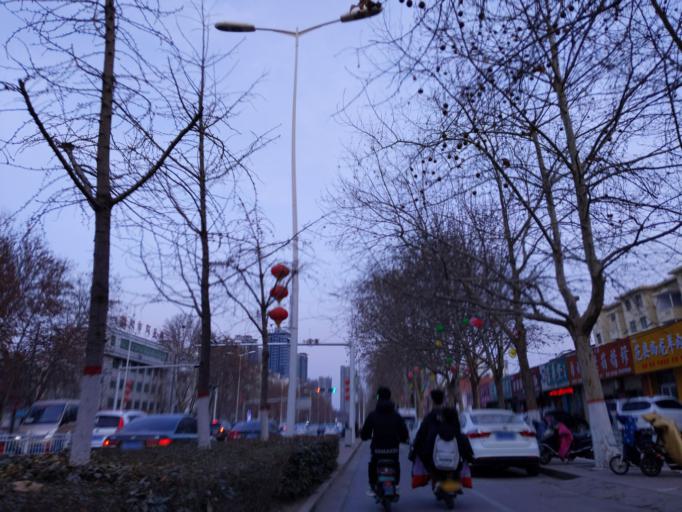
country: CN
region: Henan Sheng
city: Zhongyuanlu
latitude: 35.7804
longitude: 115.0380
